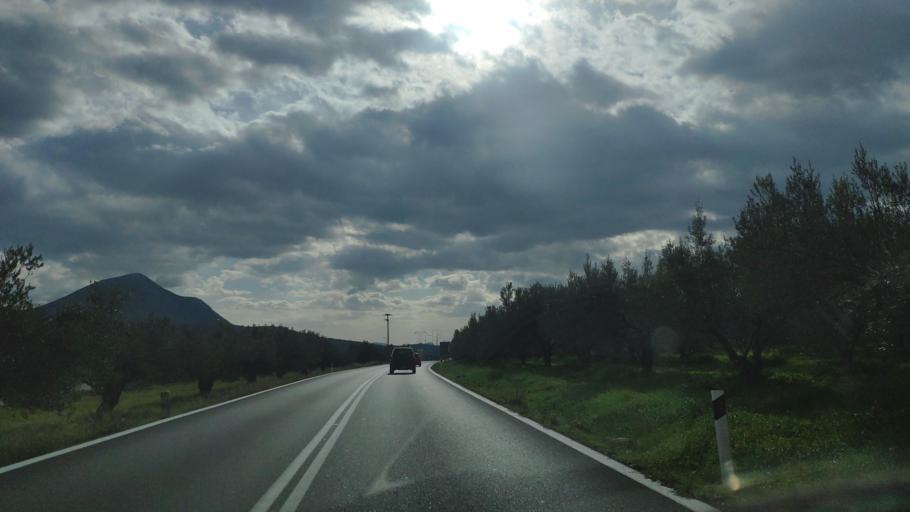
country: GR
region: Peloponnese
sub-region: Nomos Argolidos
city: Koutsopodi
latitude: 37.7575
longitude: 22.7322
